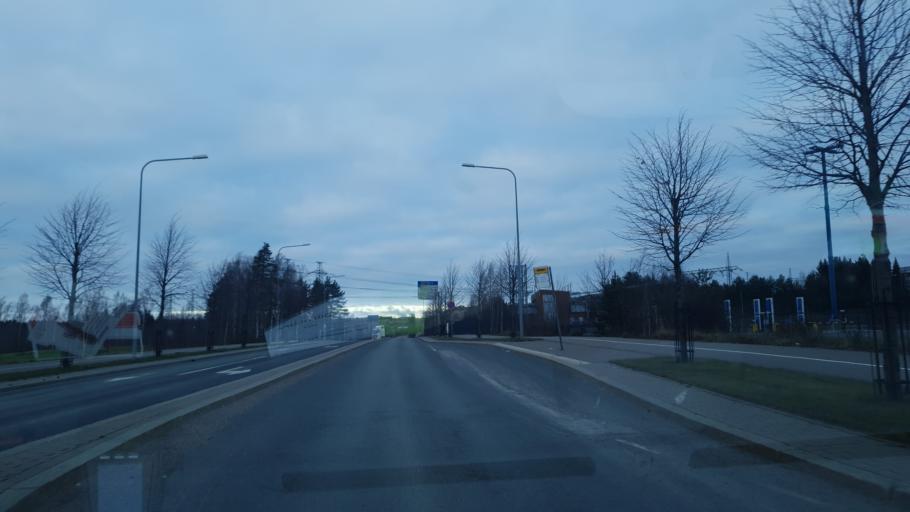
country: FI
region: Uusimaa
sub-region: Helsinki
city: Vantaa
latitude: 60.2164
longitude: 25.1650
